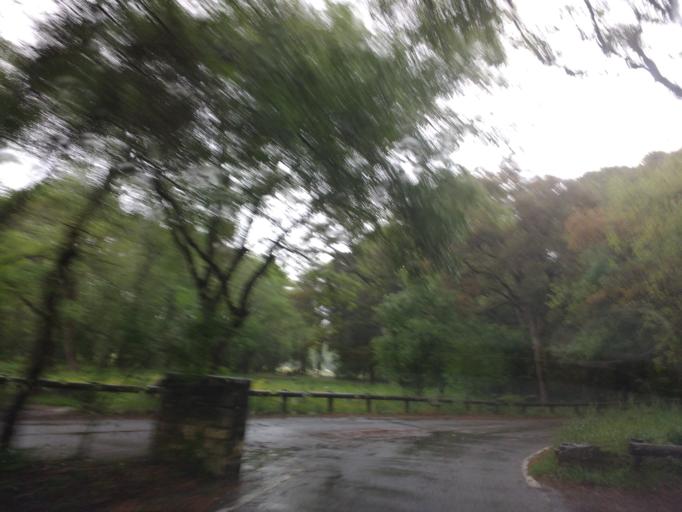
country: FR
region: Provence-Alpes-Cote d'Azur
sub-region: Departement des Alpes-Maritimes
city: Biot
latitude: 43.6262
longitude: 7.1270
